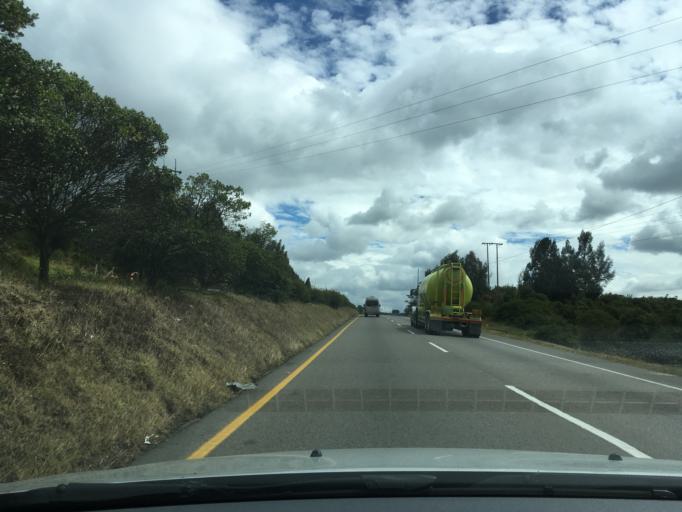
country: CO
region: Boyaca
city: Sotaquira
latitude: 5.7513
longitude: -73.1815
